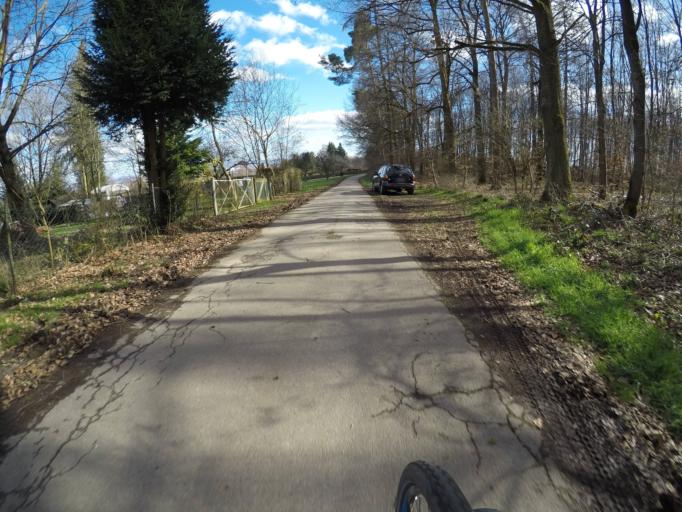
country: DE
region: Baden-Wuerttemberg
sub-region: Regierungsbezirk Stuttgart
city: Leinfelden-Echterdingen
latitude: 48.6758
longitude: 9.1572
